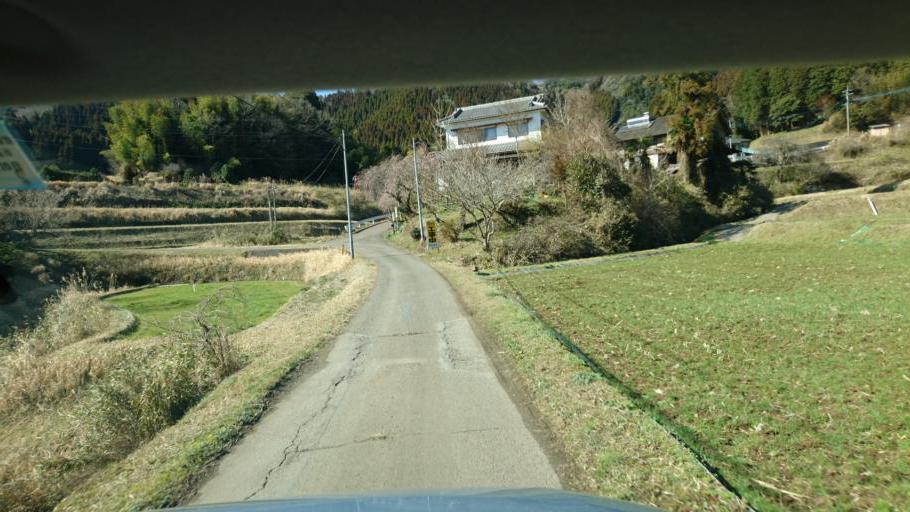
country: JP
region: Oita
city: Takedamachi
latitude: 32.7214
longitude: 131.3054
